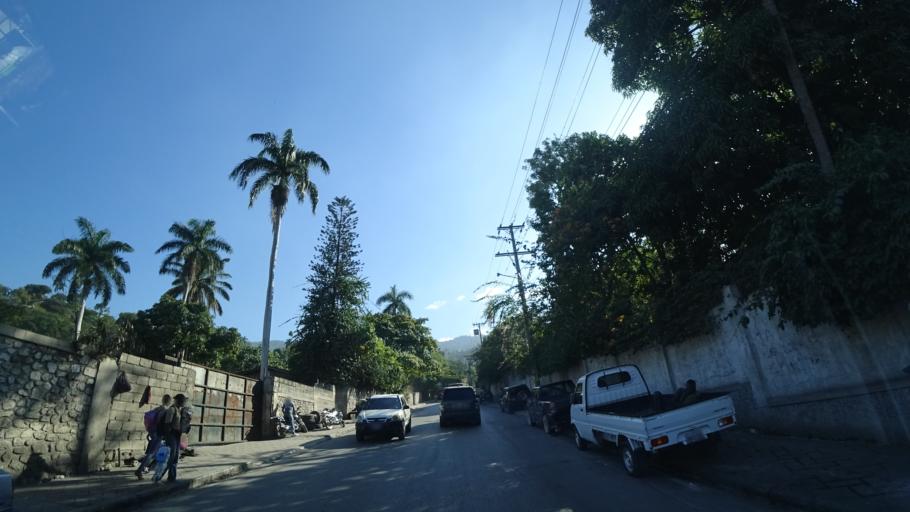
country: HT
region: Ouest
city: Petionville
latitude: 18.5099
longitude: -72.2832
